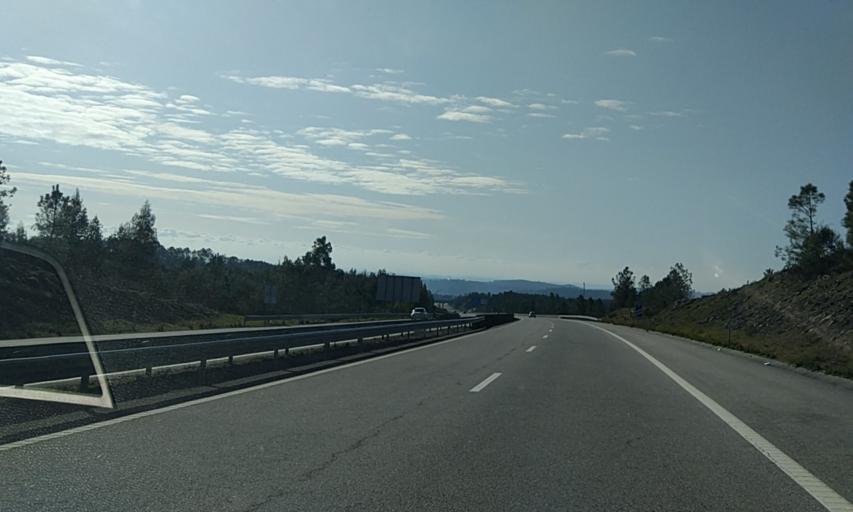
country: PT
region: Viseu
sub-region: Viseu
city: Abraveses
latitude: 40.6866
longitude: -7.9654
